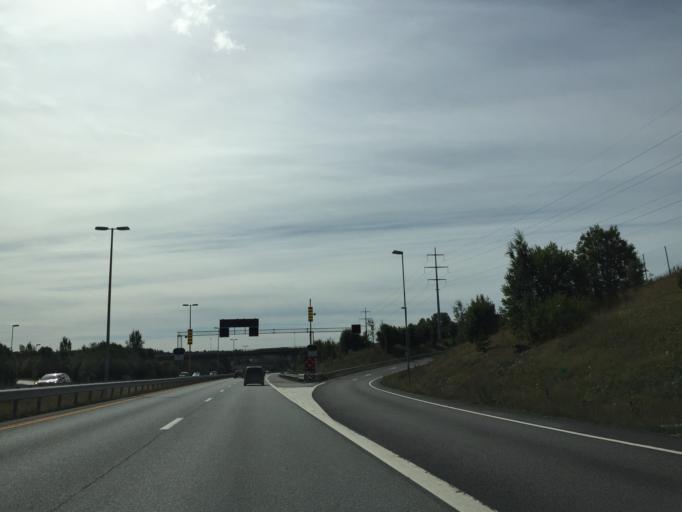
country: NO
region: Akershus
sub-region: Vestby
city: Vestby
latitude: 59.6050
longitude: 10.7364
